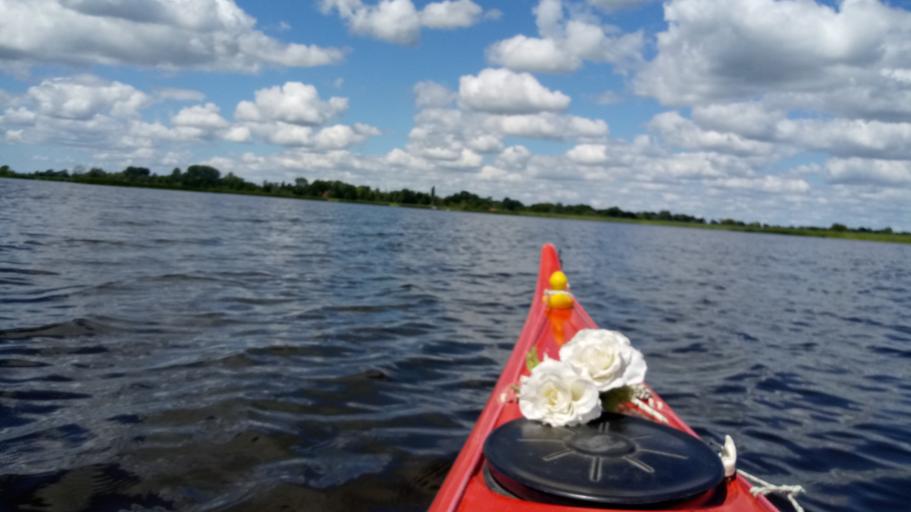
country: NL
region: Overijssel
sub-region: Gemeente Steenwijkerland
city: Giethoorn
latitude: 52.7019
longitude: 6.0840
